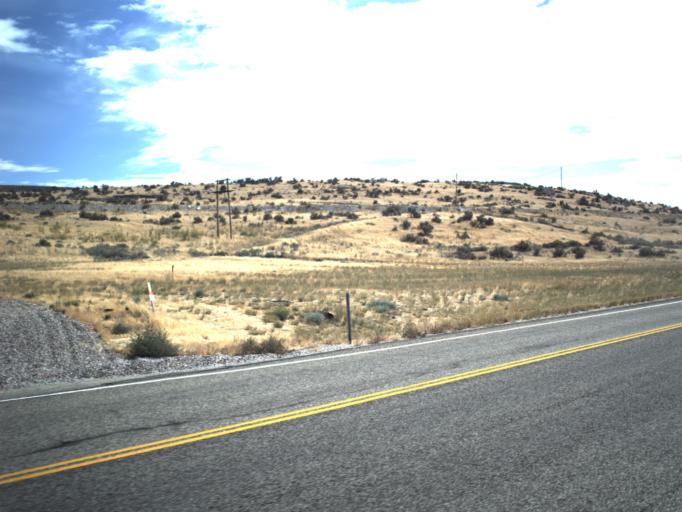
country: US
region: Utah
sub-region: Box Elder County
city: Tremonton
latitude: 41.6576
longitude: -112.4413
